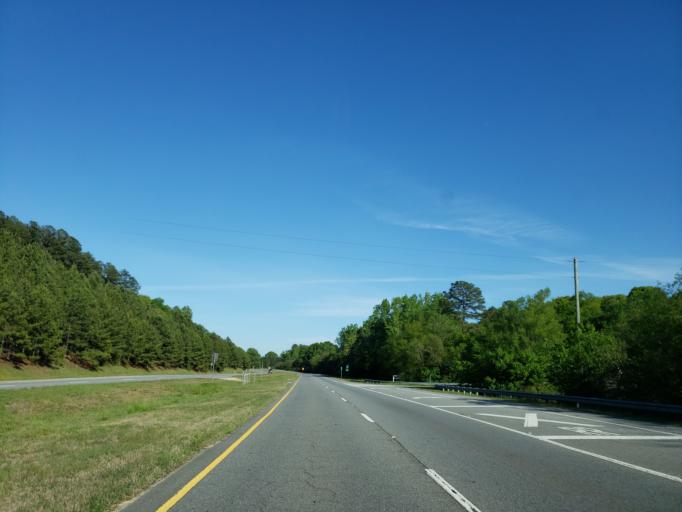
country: US
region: Georgia
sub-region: Polk County
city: Cedartown
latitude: 34.0054
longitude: -85.1735
